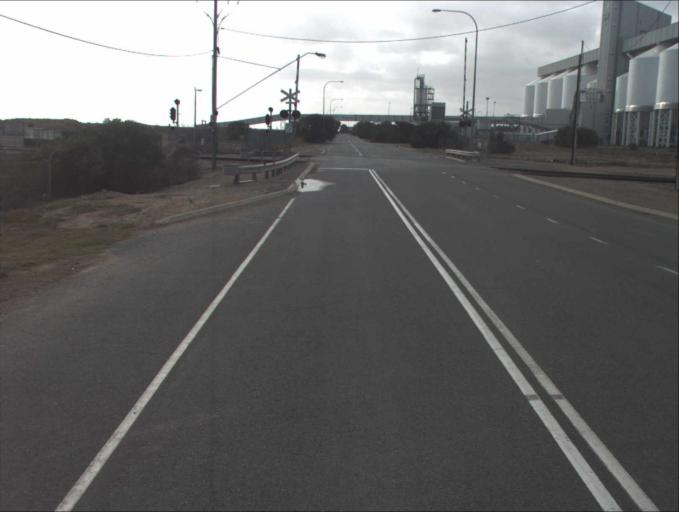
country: AU
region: South Australia
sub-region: Port Adelaide Enfield
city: Birkenhead
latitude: -34.7735
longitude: 138.5015
